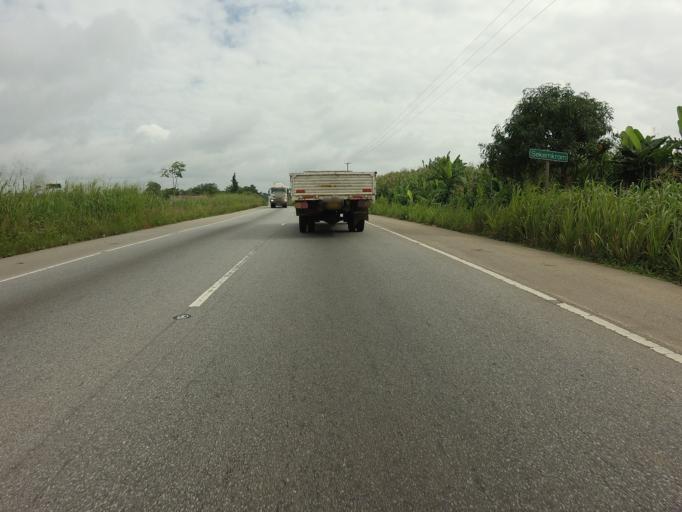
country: GH
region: Ashanti
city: Tafo
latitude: 6.9851
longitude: -1.6886
